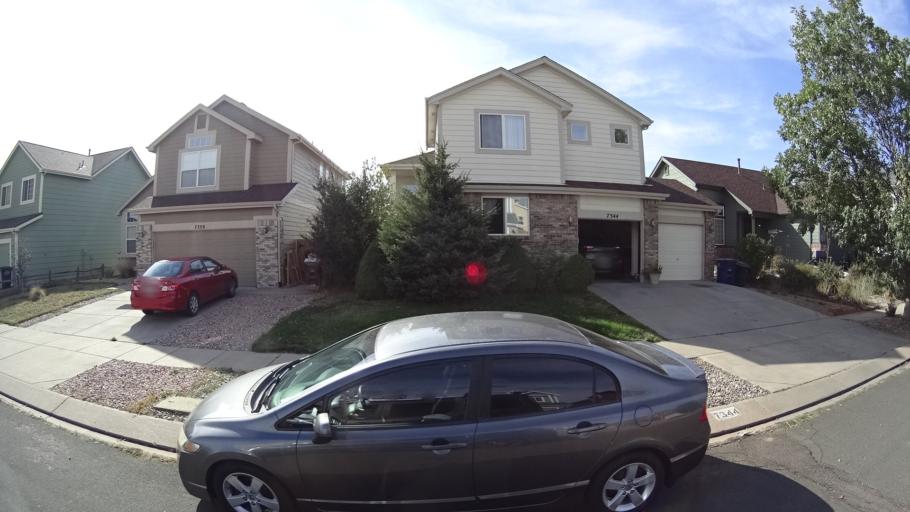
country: US
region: Colorado
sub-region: El Paso County
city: Cimarron Hills
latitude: 38.9066
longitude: -104.6911
